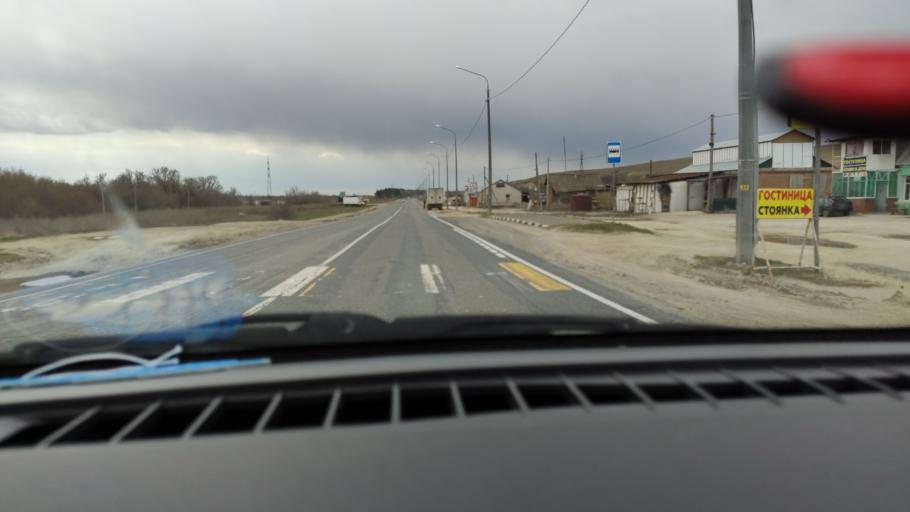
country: RU
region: Saratov
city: Sinodskoye
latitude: 52.0823
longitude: 46.7973
